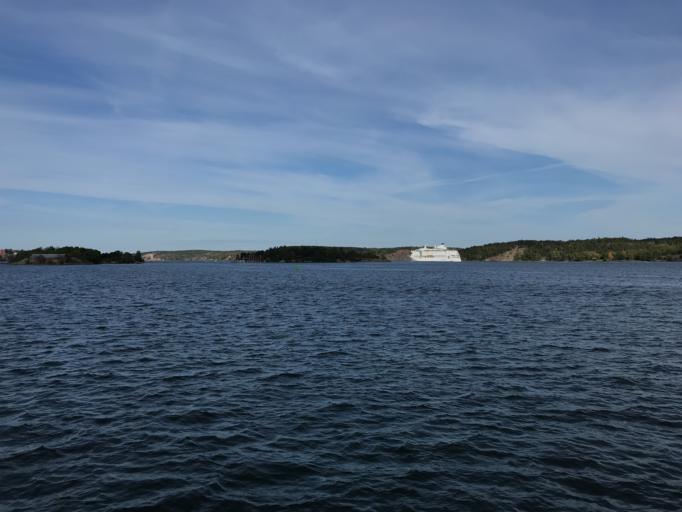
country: SE
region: Stockholm
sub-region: Nacka Kommun
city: Nacka
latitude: 59.3274
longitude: 18.1572
